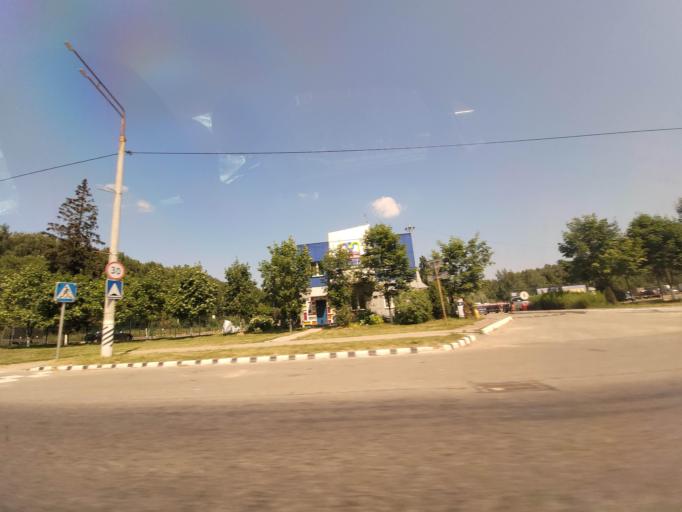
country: RU
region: Kaluga
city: Obninsk
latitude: 55.1248
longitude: 36.6200
